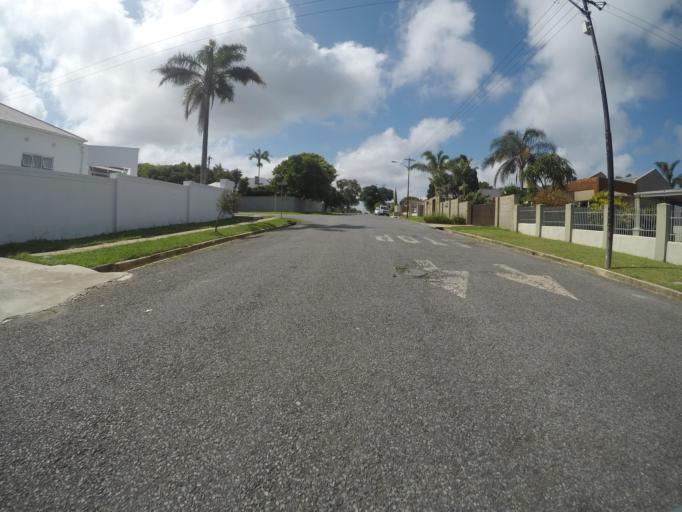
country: ZA
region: Eastern Cape
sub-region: Buffalo City Metropolitan Municipality
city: East London
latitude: -32.9805
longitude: 27.9048
